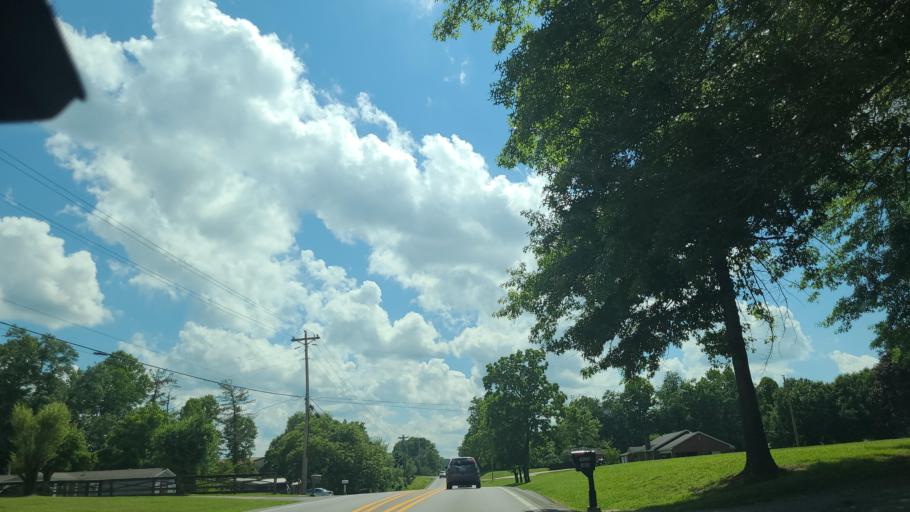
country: US
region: Kentucky
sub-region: Whitley County
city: Corbin
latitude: 36.9058
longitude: -84.1610
